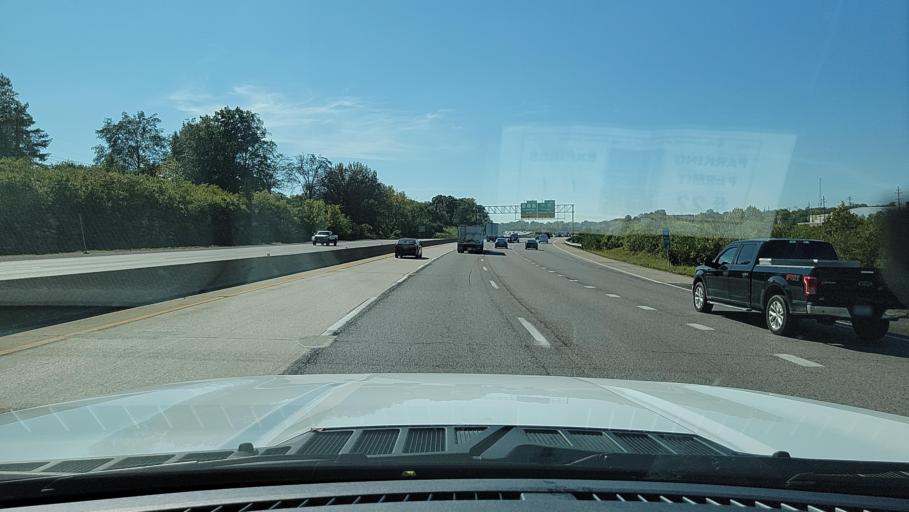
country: US
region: Missouri
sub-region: Saint Louis County
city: Mehlville
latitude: 38.5221
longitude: -90.3232
